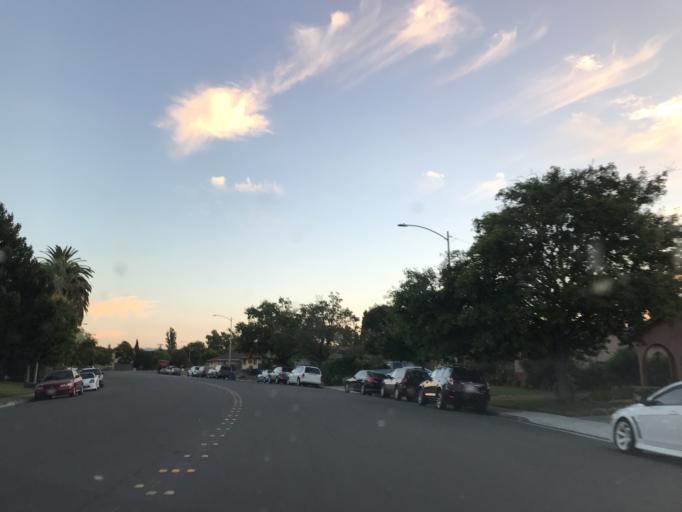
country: US
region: California
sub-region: Santa Clara County
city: Milpitas
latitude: 37.4361
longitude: -121.9115
